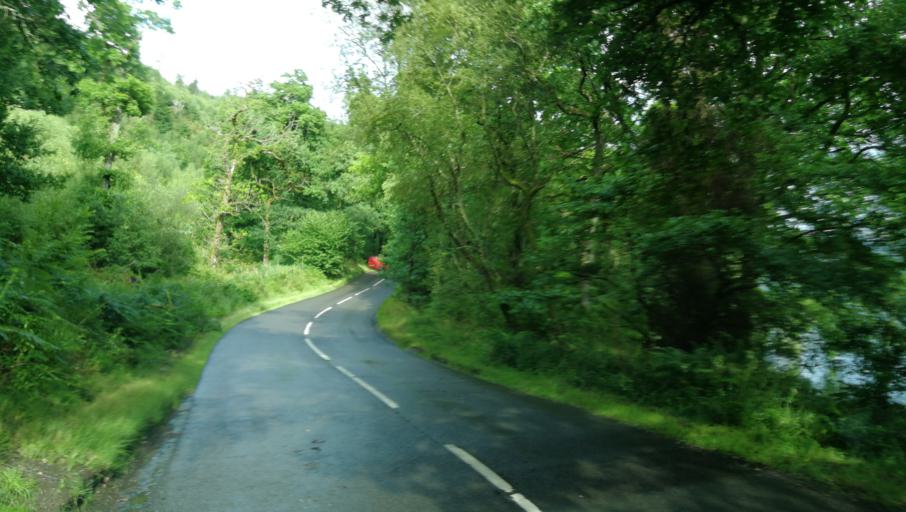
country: GB
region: Scotland
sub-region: Stirling
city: Callander
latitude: 56.2268
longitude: -4.3185
